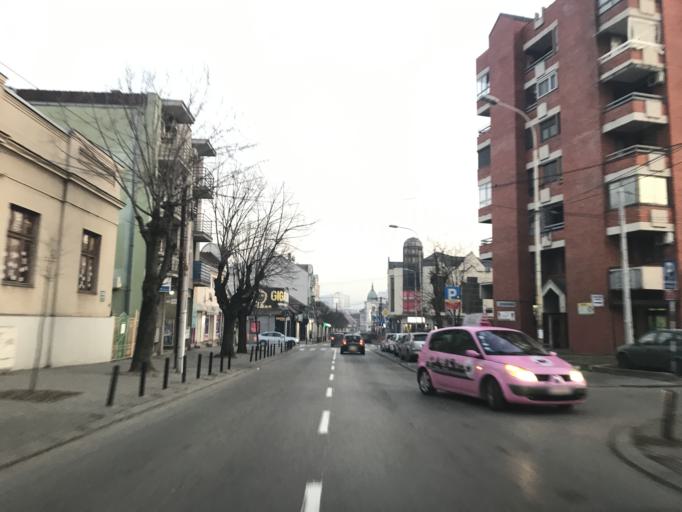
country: RS
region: Central Serbia
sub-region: Sumadijski Okrug
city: Kragujevac
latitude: 44.0143
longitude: 20.9129
